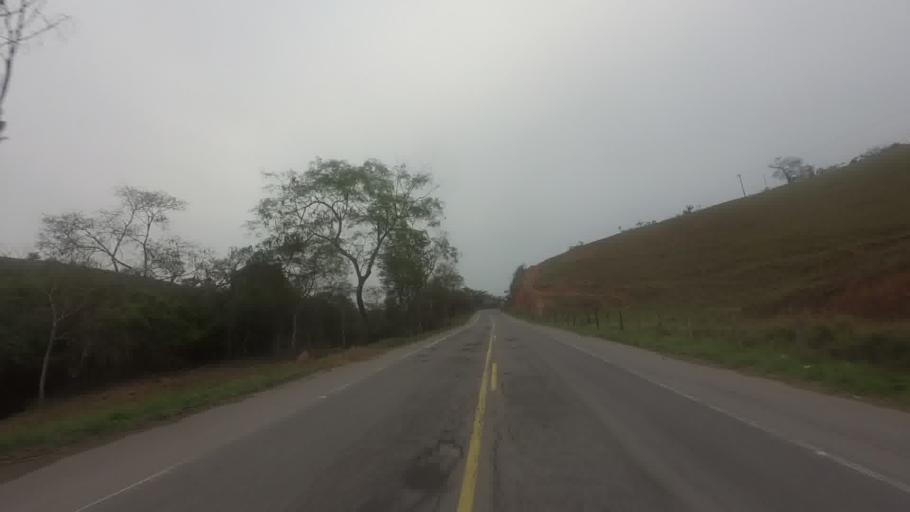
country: BR
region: Rio de Janeiro
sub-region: Santo Antonio De Padua
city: Santo Antonio de Padua
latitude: -21.6562
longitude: -42.3034
